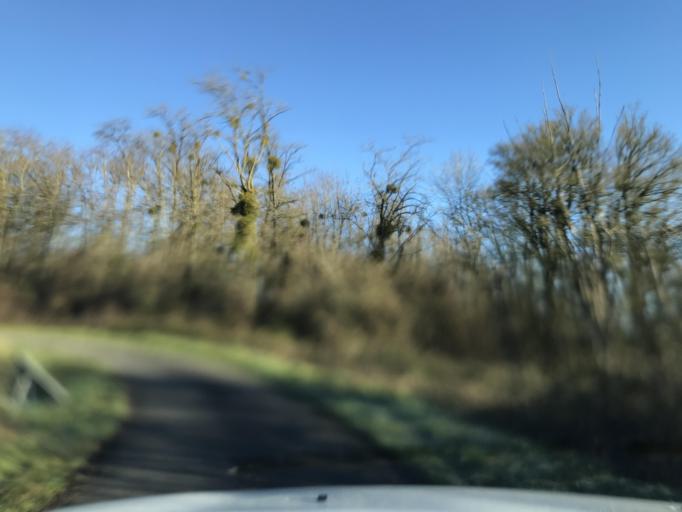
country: FR
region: Poitou-Charentes
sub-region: Departement de la Charente
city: Chasseneuil-sur-Bonnieure
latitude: 45.8384
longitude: 0.5051
